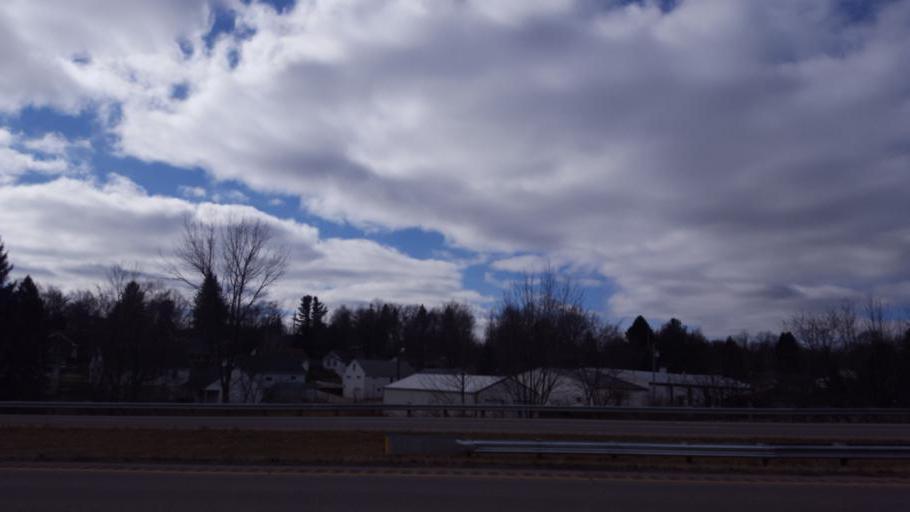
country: US
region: Ohio
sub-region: Richland County
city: Mansfield
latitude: 40.7386
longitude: -82.5117
